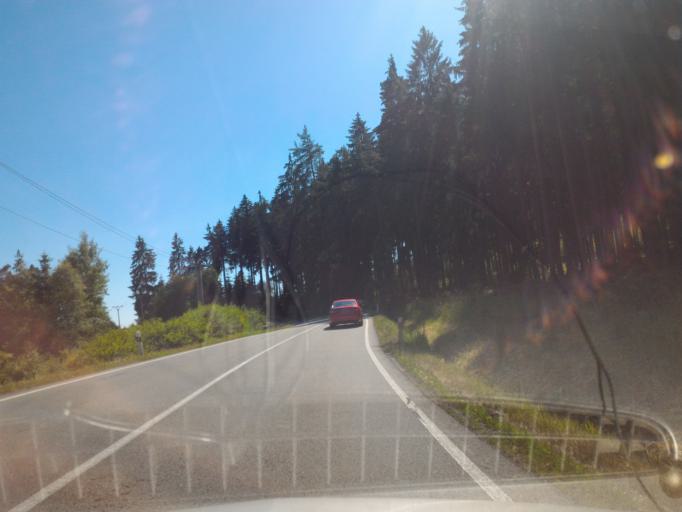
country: CZ
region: Vysocina
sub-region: Okres Jihlava
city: Trest'
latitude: 49.2508
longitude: 15.4694
